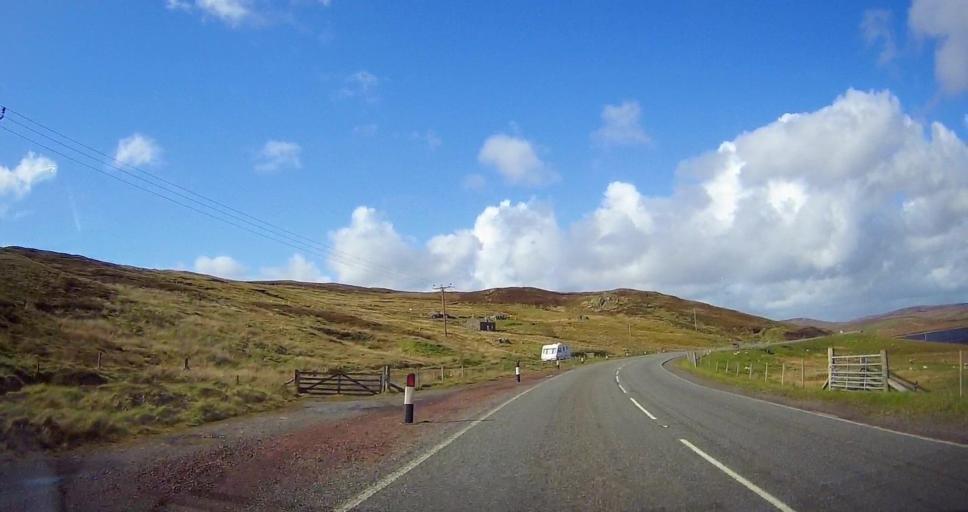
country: GB
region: Scotland
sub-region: Shetland Islands
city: Lerwick
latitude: 60.2545
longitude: -1.2267
